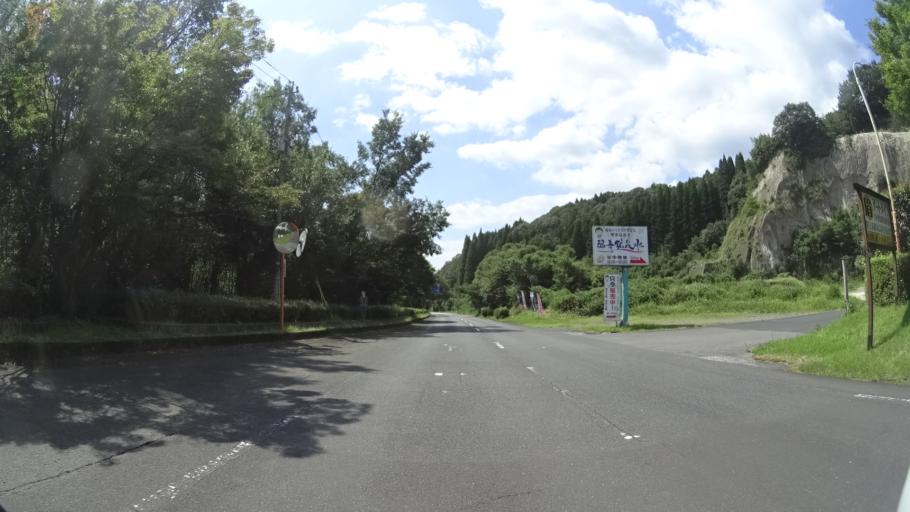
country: JP
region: Kagoshima
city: Kokubu-matsuki
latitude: 31.8594
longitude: 130.7781
